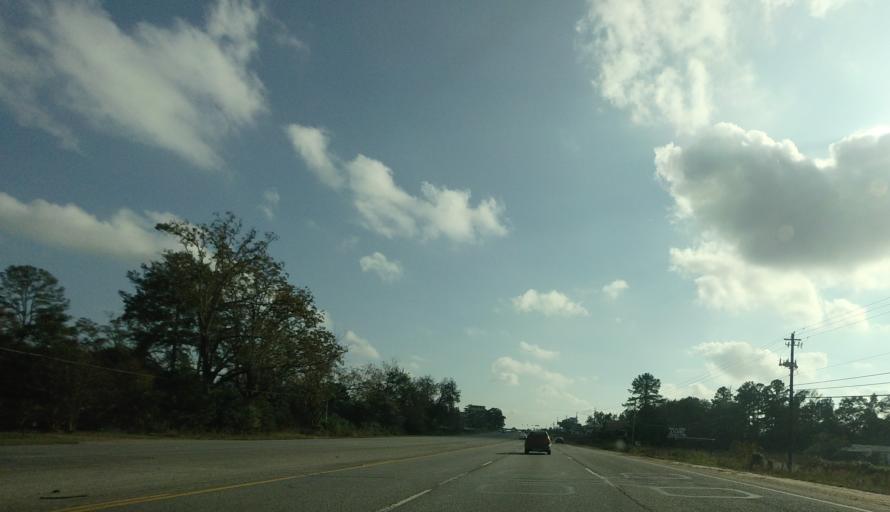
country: US
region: Georgia
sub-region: Bibb County
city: Macon
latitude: 32.7362
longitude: -83.6559
